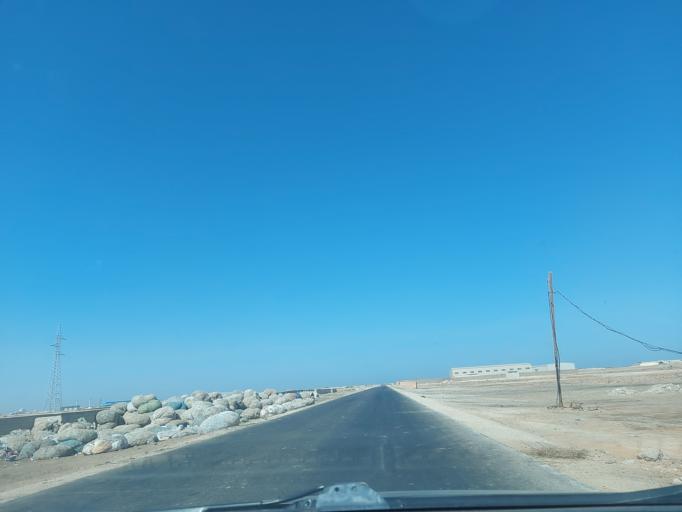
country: MR
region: Nouakchott
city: Nouakchott
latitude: 18.0596
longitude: -16.0098
